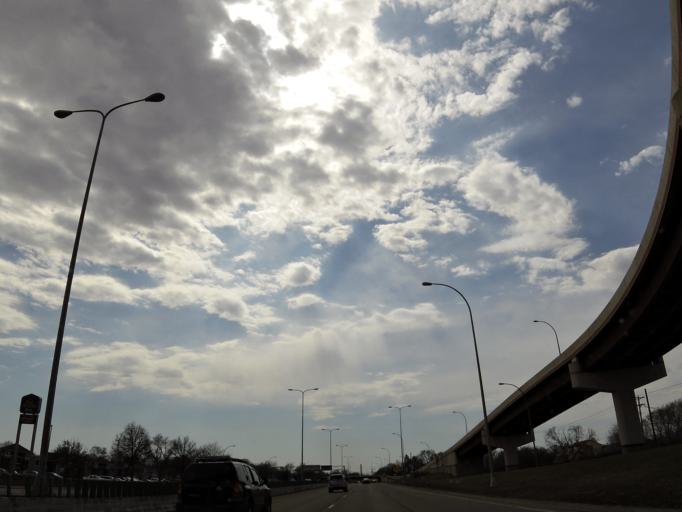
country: US
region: Minnesota
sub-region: Hennepin County
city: Richfield
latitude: 44.8523
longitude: -93.2474
